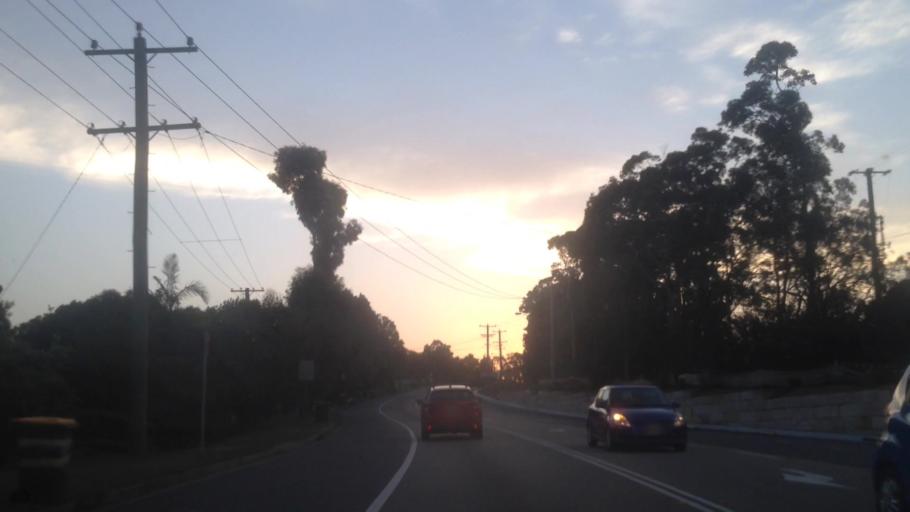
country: AU
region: New South Wales
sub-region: Lake Macquarie Shire
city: Dora Creek
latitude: -33.1062
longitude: 151.4969
